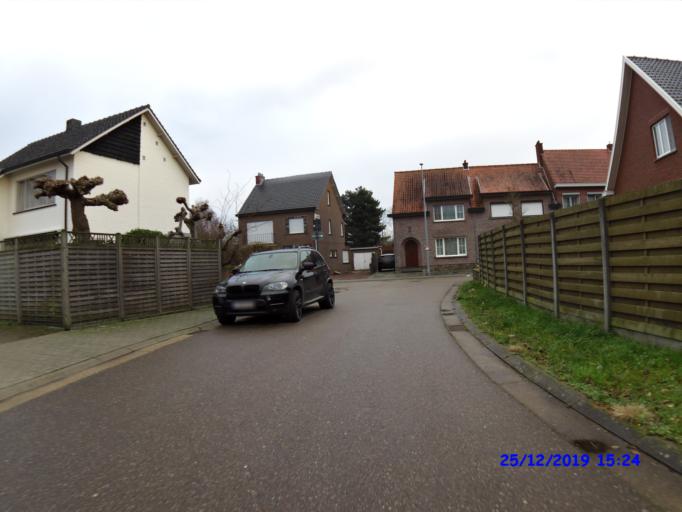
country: BE
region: Flanders
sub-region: Provincie Antwerpen
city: Geel
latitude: 51.1699
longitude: 4.9828
